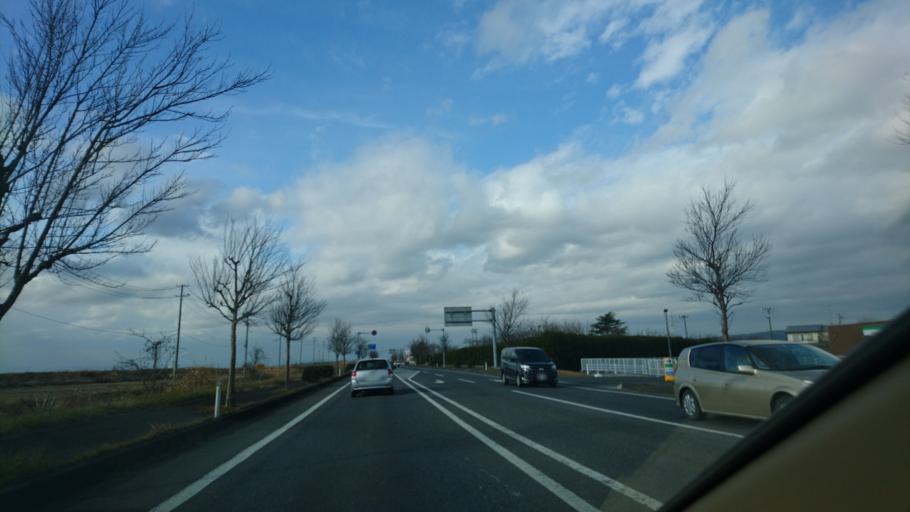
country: JP
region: Miyagi
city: Wakuya
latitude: 38.5341
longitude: 141.1218
